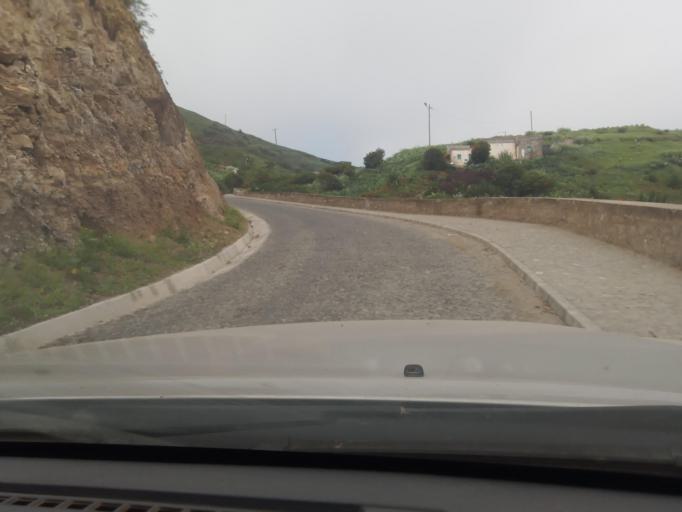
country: CV
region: Brava
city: Vila Nova Sintra
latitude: 14.8717
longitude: -24.7006
